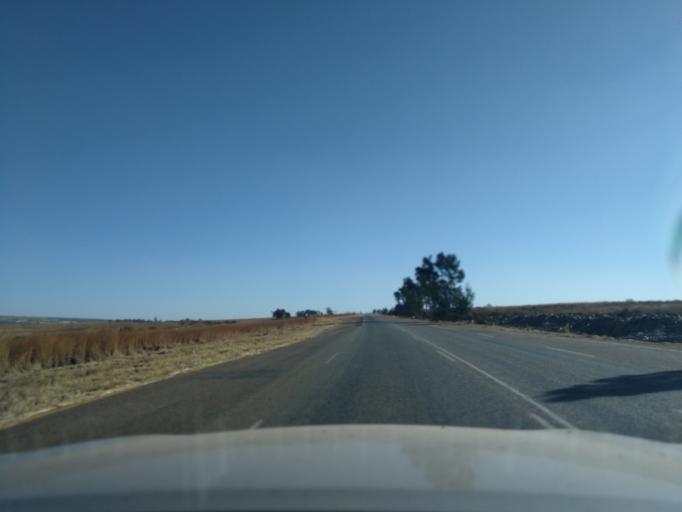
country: ZA
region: Gauteng
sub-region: West Rand District Municipality
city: Randfontein
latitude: -25.9981
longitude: 27.5102
